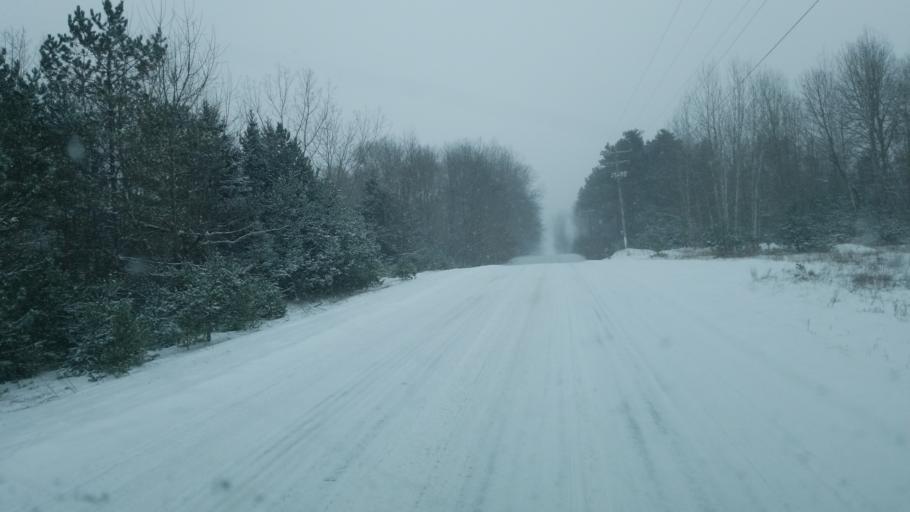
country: US
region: Michigan
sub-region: Mecosta County
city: Canadian Lakes
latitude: 43.5904
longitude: -85.3012
